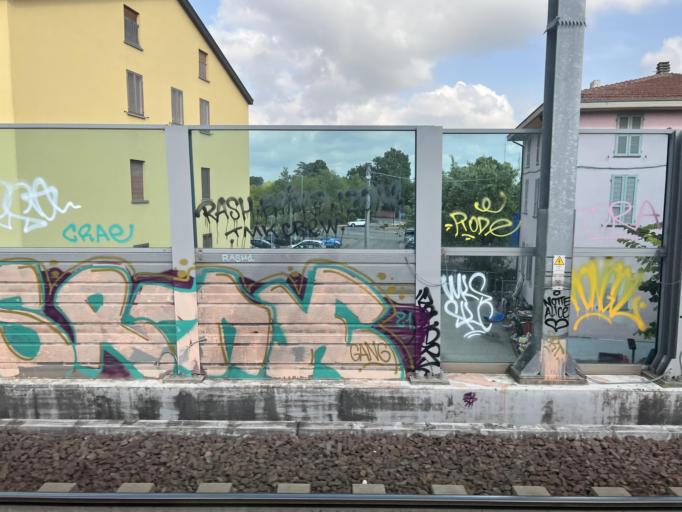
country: IT
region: Emilia-Romagna
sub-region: Provincia di Parma
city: Parma
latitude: 44.8111
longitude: 10.3469
